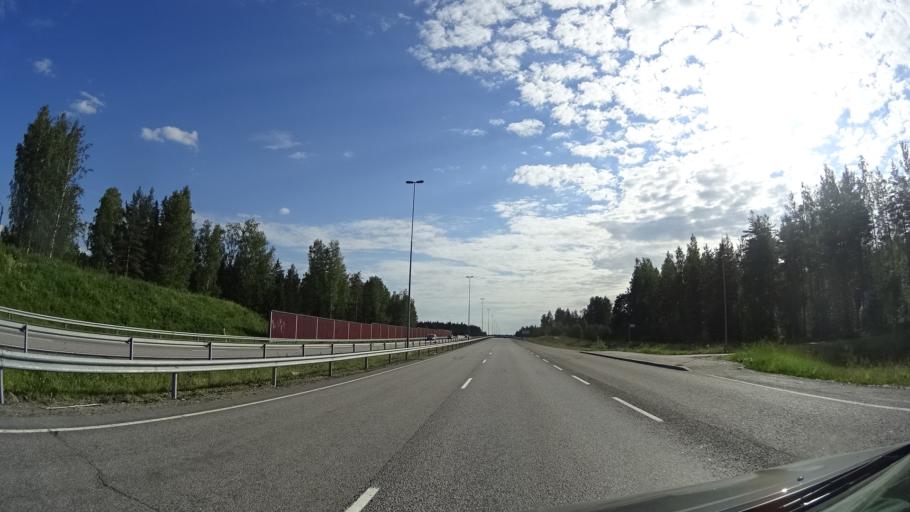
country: FI
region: South Karelia
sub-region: Lappeenranta
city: Joutseno
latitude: 61.0928
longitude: 28.3659
